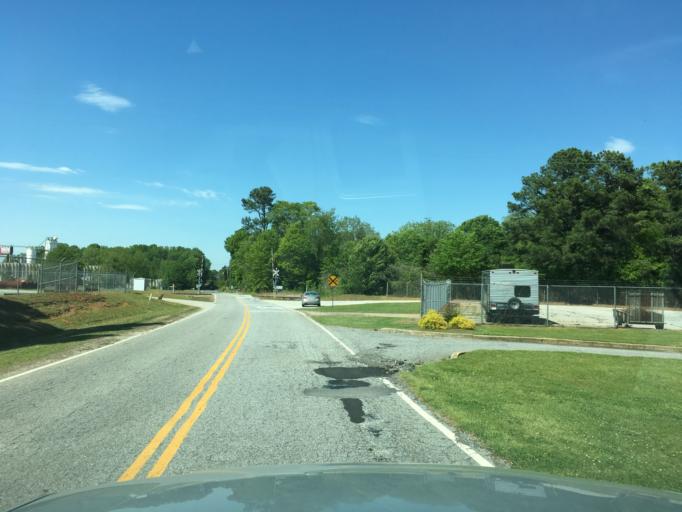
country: US
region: South Carolina
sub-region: Spartanburg County
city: Southern Shops
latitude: 34.9922
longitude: -82.0186
